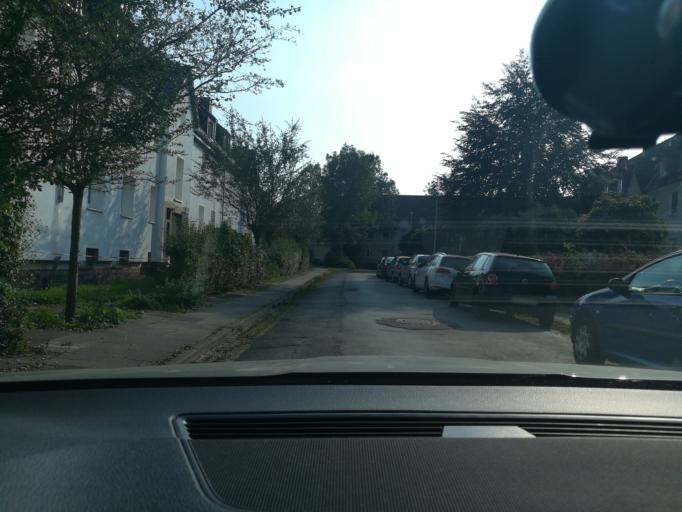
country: DE
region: North Rhine-Westphalia
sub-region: Regierungsbezirk Detmold
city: Minden
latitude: 52.2975
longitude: 8.9196
